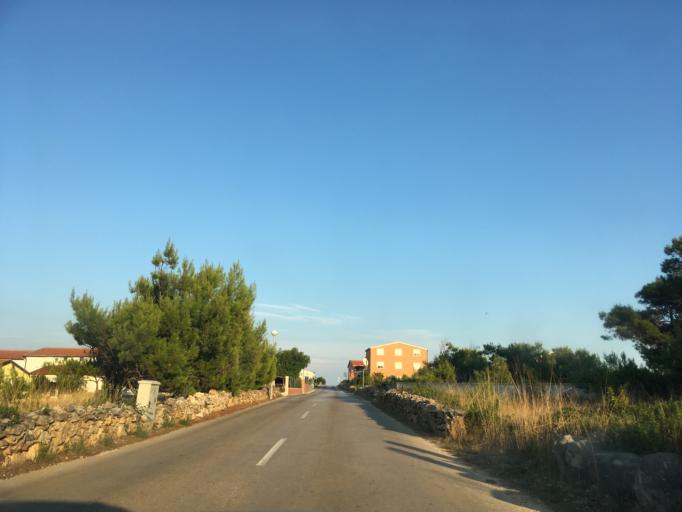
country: HR
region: Zadarska
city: Vir
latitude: 44.2999
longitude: 15.1117
